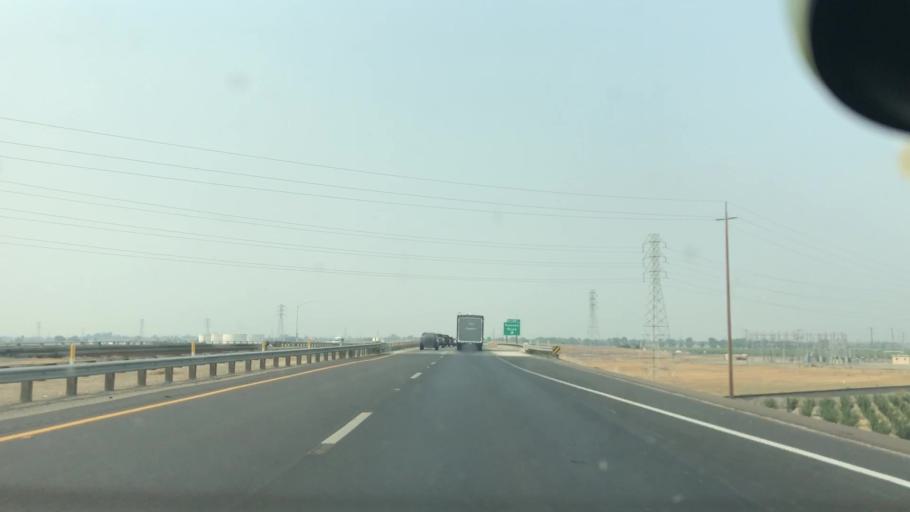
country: US
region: California
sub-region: San Joaquin County
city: Tracy
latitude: 37.7417
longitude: -121.3435
